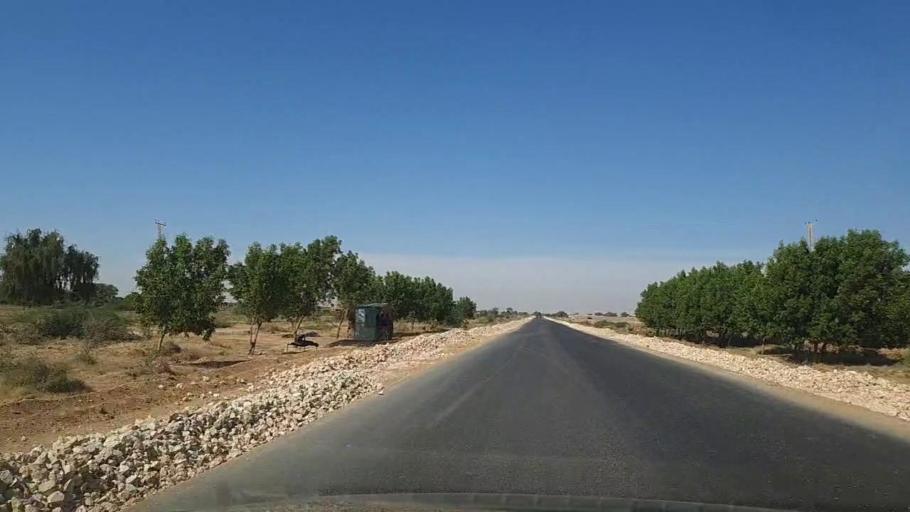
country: PK
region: Sindh
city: Kotri
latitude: 25.2739
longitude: 68.2156
